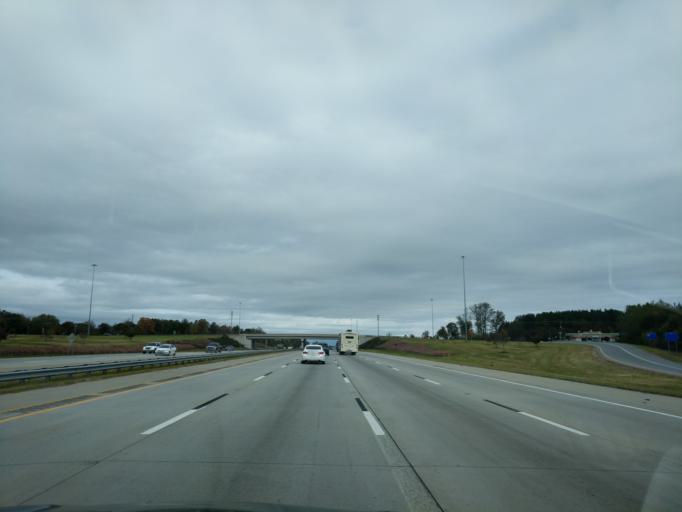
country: US
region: North Carolina
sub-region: Rowan County
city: East Spencer
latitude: 35.6917
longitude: -80.4022
